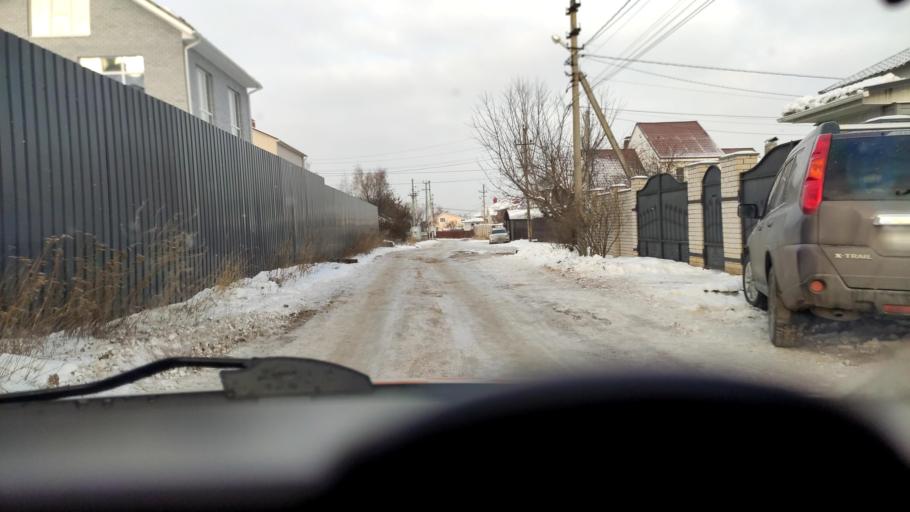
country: RU
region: Voronezj
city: Podgornoye
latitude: 51.7270
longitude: 39.1608
